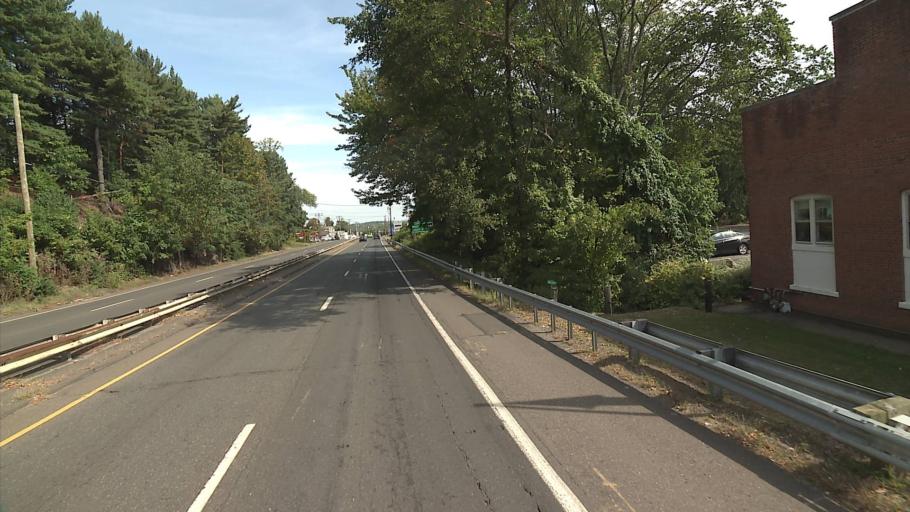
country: US
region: Connecticut
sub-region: New Haven County
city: West Haven
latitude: 41.3056
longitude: -72.9726
